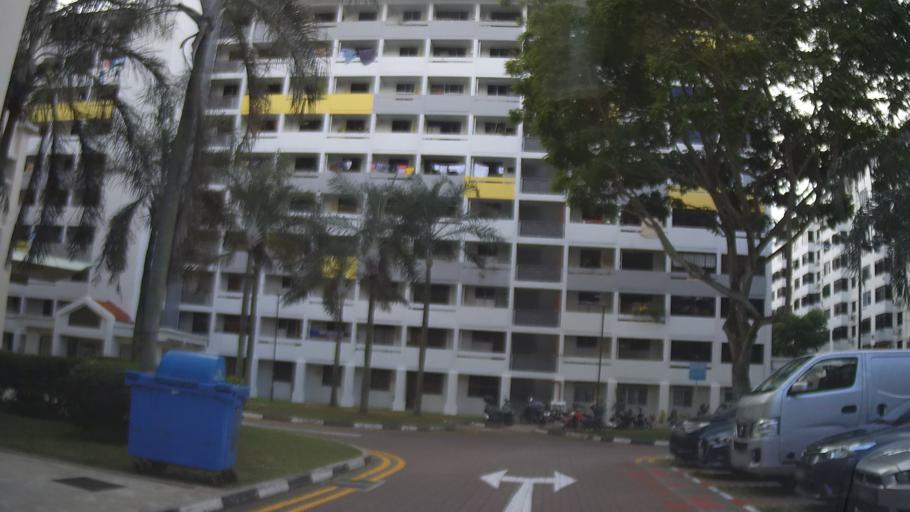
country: SG
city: Singapore
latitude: 1.3271
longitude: 103.8860
